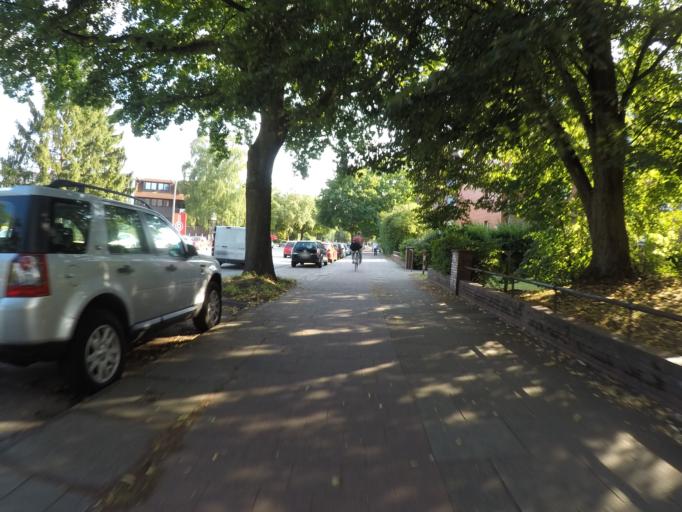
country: DE
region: Hamburg
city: Steilshoop
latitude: 53.6004
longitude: 10.0678
